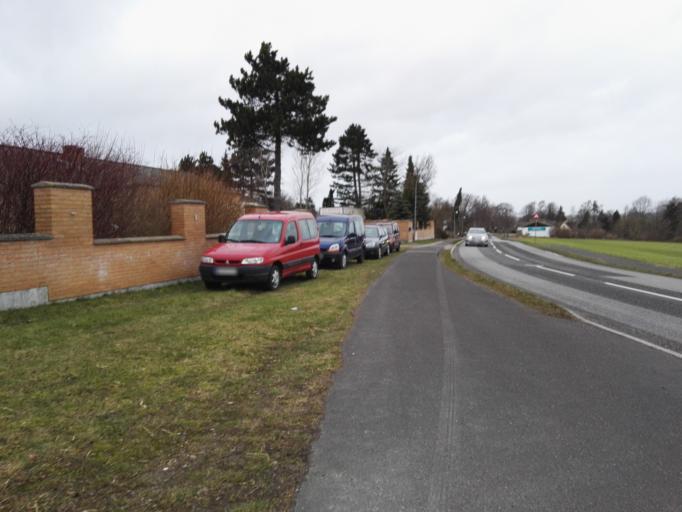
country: DK
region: Zealand
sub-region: Lejre Kommune
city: Ejby
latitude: 55.6893
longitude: 11.9122
